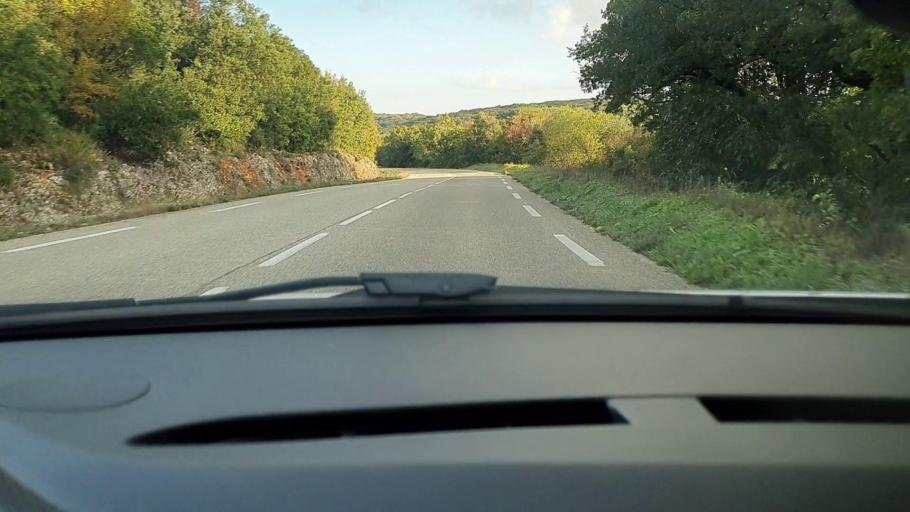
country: FR
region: Languedoc-Roussillon
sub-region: Departement du Gard
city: Barjac
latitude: 44.2232
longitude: 4.3198
